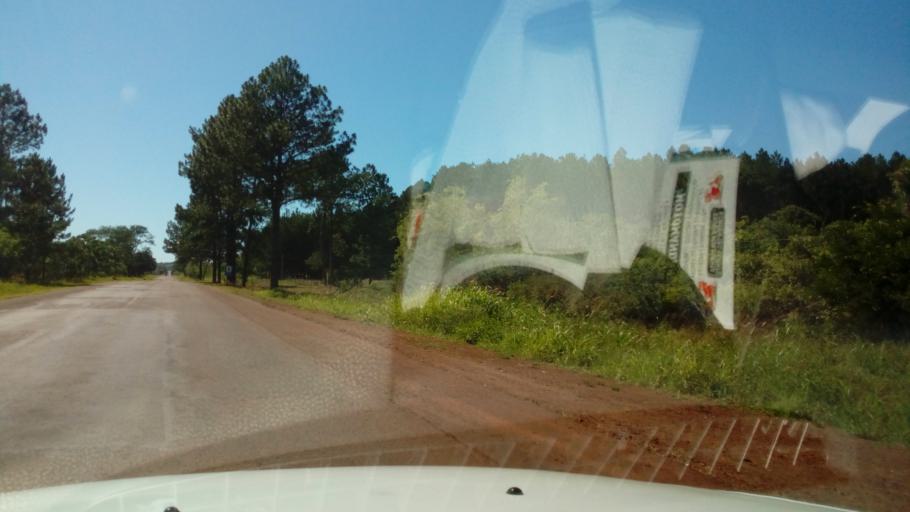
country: AR
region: Misiones
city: Almafuerte
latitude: -27.5669
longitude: -55.4006
